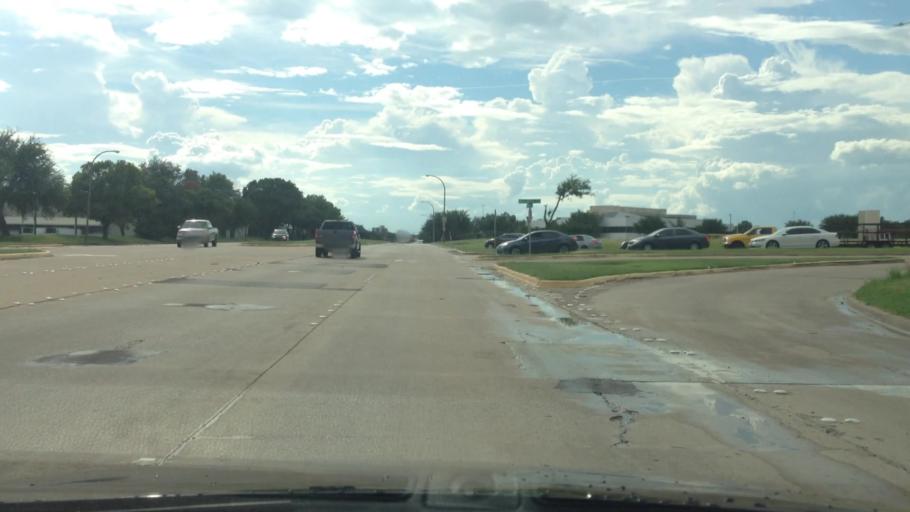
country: US
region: Texas
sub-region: Tarrant County
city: Haltom City
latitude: 32.8244
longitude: -97.2993
